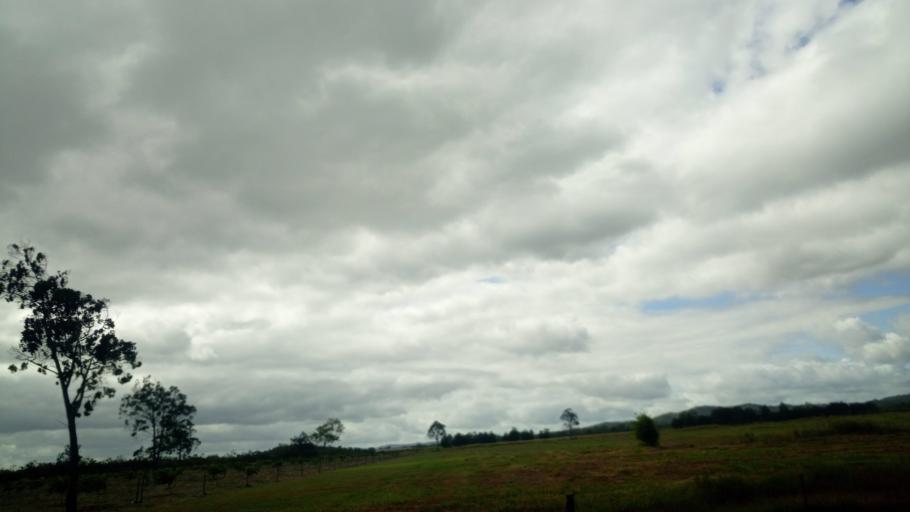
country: AU
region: Queensland
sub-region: Tablelands
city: Mareeba
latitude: -16.9668
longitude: 145.4479
